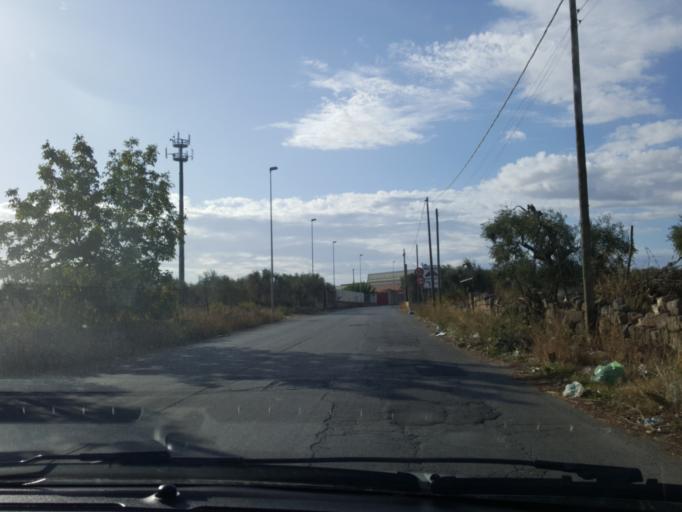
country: IT
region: Apulia
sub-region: Provincia di Bari
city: Triggiano
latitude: 41.0628
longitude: 16.9350
